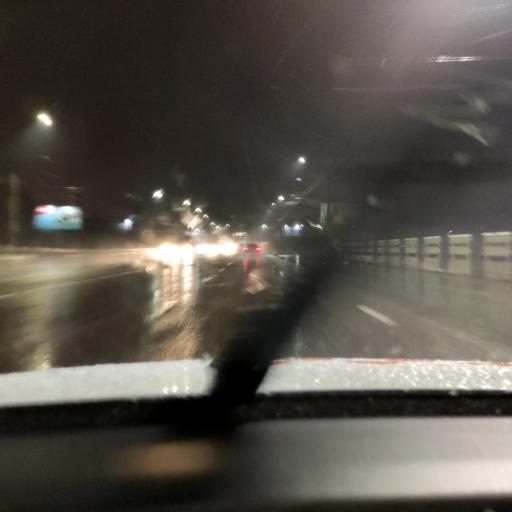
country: RU
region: Voronezj
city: Voronezh
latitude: 51.6335
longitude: 39.2239
